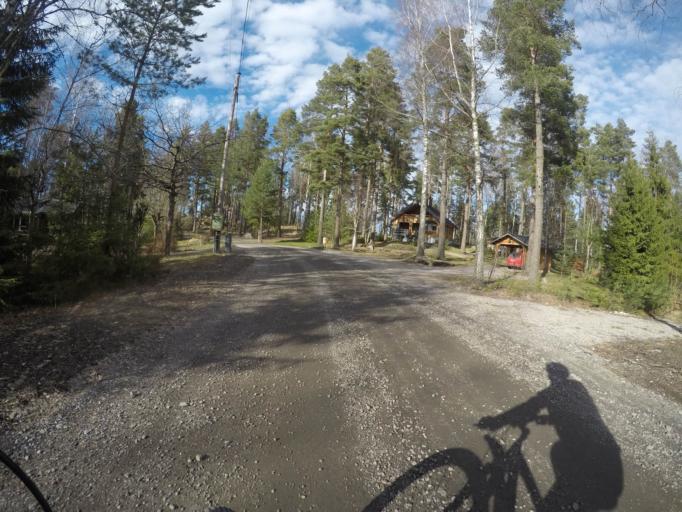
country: SE
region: Vaestmanland
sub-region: Kungsors Kommun
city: Kungsoer
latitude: 59.4337
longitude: 16.1414
